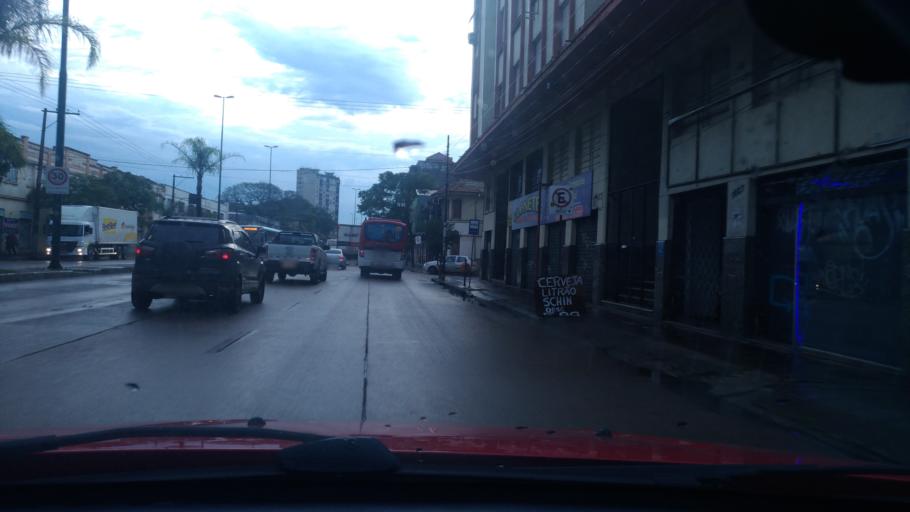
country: BR
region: Rio Grande do Sul
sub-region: Porto Alegre
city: Porto Alegre
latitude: -30.0171
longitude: -51.2080
